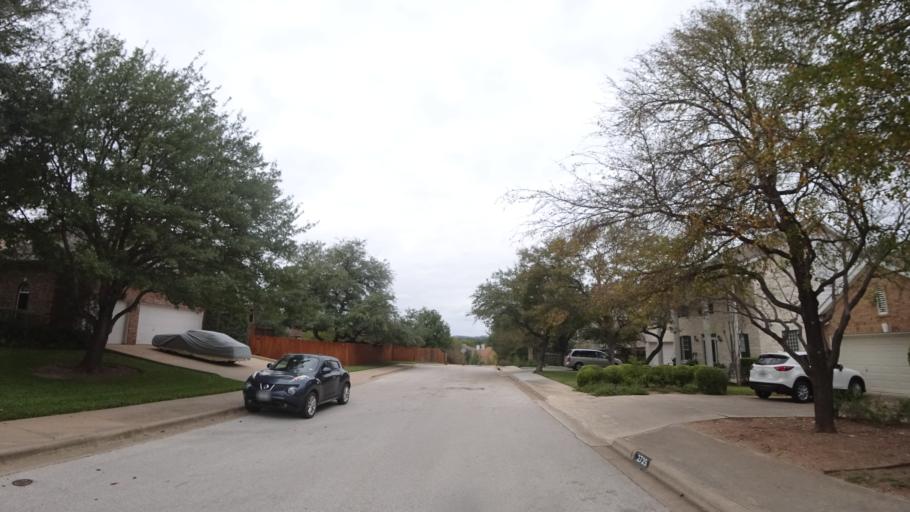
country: US
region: Texas
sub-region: Travis County
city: Bee Cave
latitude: 30.3130
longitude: -97.9218
